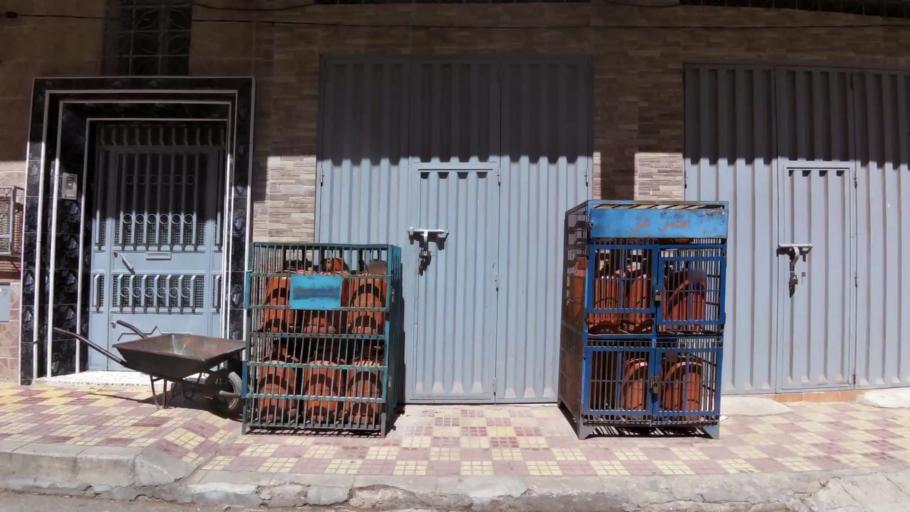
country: MA
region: Tanger-Tetouan
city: Tetouan
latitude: 35.5795
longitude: -5.3471
